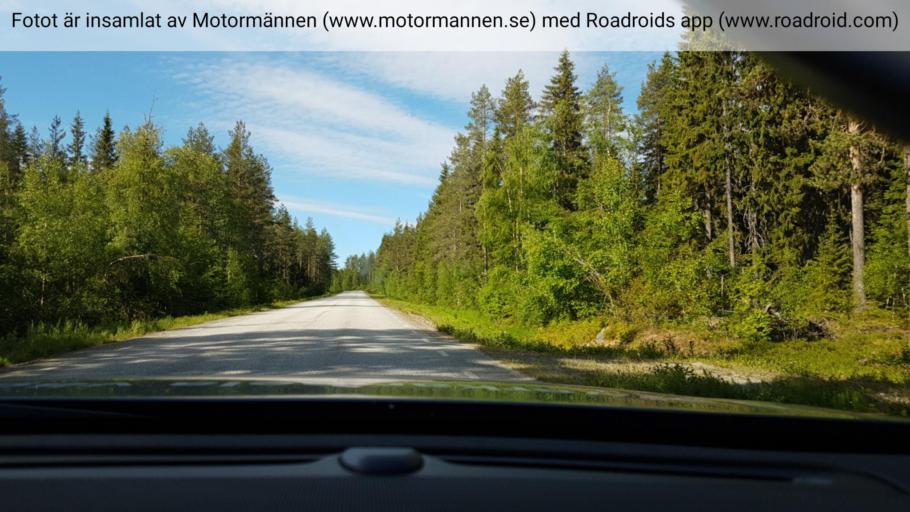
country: SE
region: Vaesterbotten
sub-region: Bjurholms Kommun
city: Bjurholm
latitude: 63.9747
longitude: 19.3151
